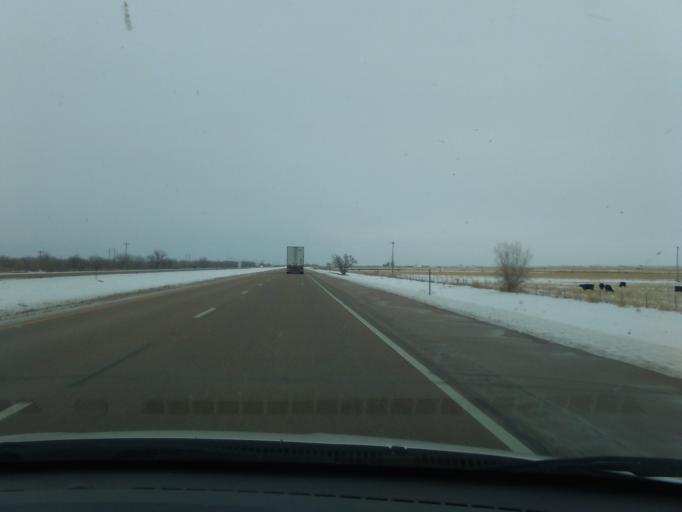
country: US
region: Nebraska
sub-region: Keith County
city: Ogallala
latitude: 41.0828
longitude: -101.8713
